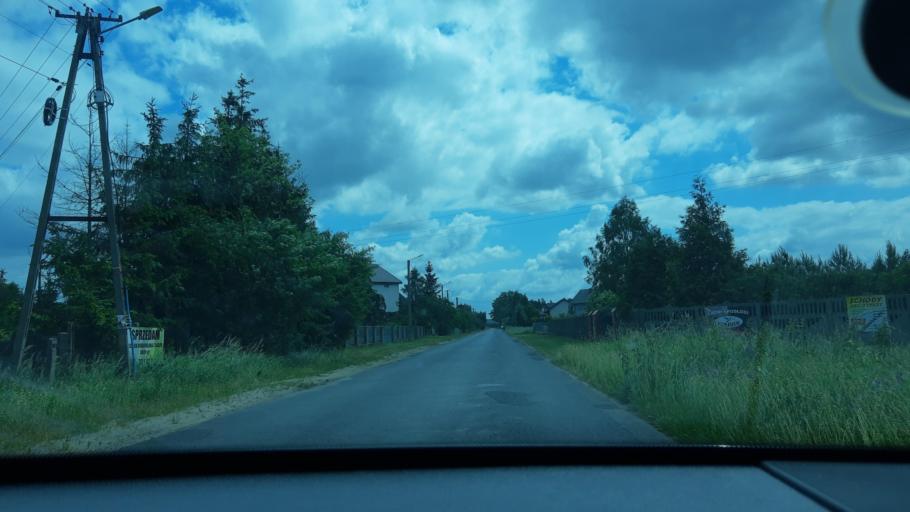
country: PL
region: Lodz Voivodeship
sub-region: Powiat zdunskowolski
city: Zapolice
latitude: 51.5402
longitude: 18.8012
